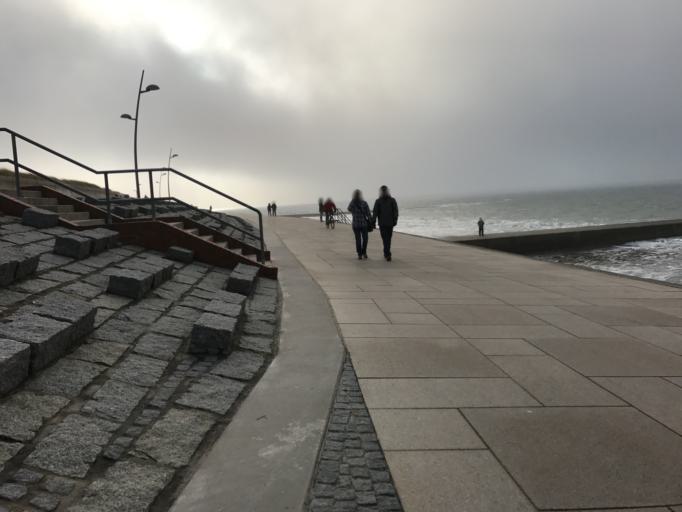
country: DE
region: Lower Saxony
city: Borkum
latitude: 53.5856
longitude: 6.6570
